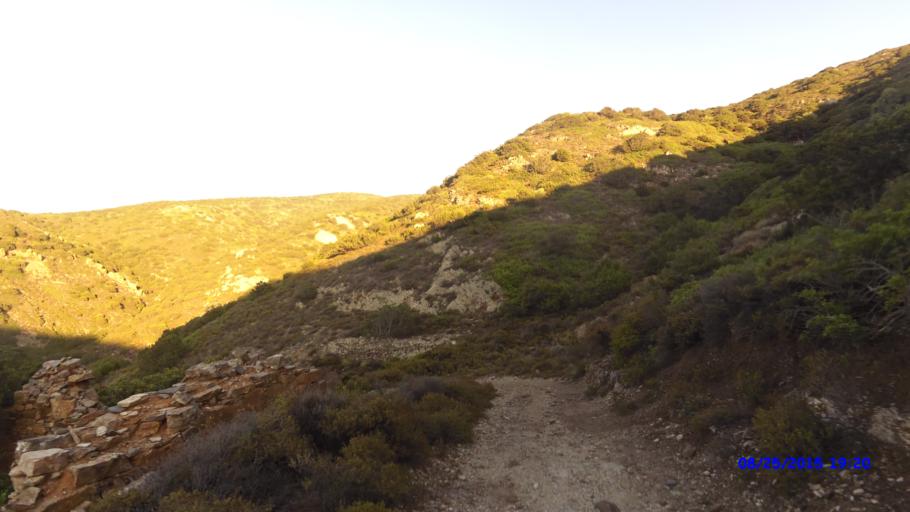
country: GR
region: South Aegean
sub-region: Nomos Kykladon
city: Antiparos
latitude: 36.9973
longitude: 25.0395
